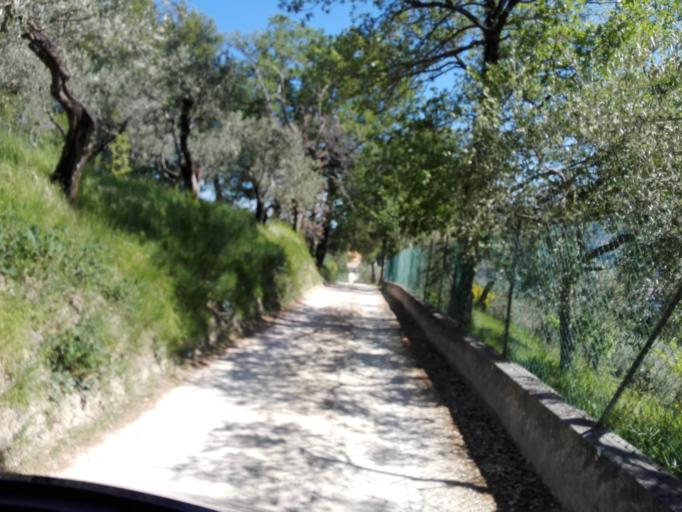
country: IT
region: Umbria
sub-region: Provincia di Perugia
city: Foligno
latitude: 42.9734
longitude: 12.7411
